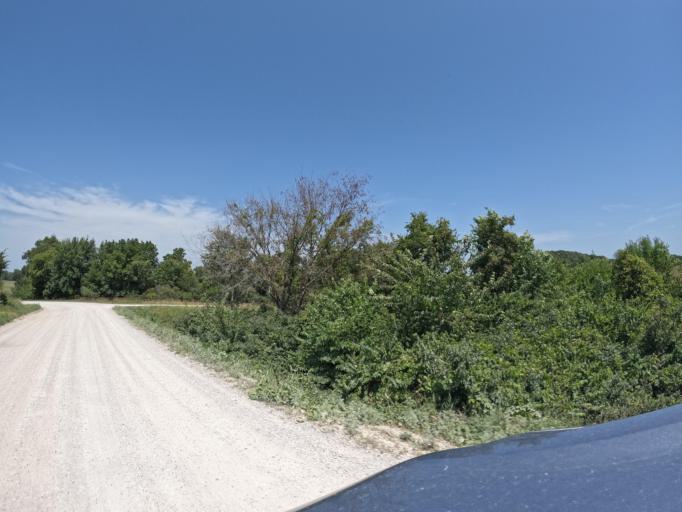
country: US
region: Iowa
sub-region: Henry County
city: Mount Pleasant
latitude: 40.9644
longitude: -91.6726
